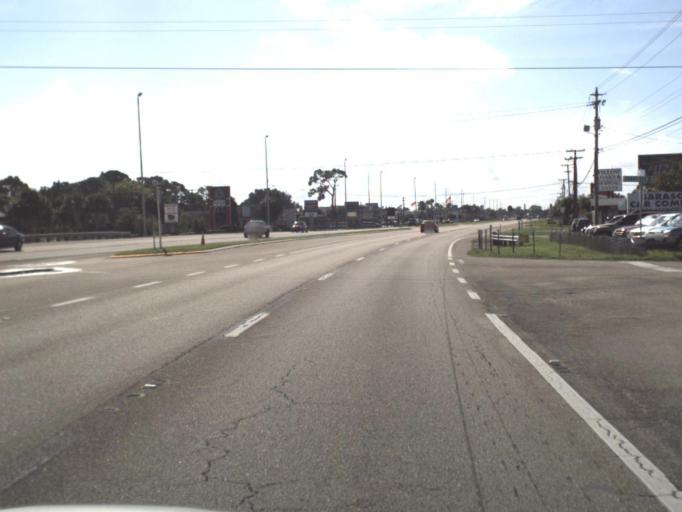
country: US
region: Florida
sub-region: Sarasota County
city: Gulf Gate Estates
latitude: 27.2522
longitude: -82.5152
